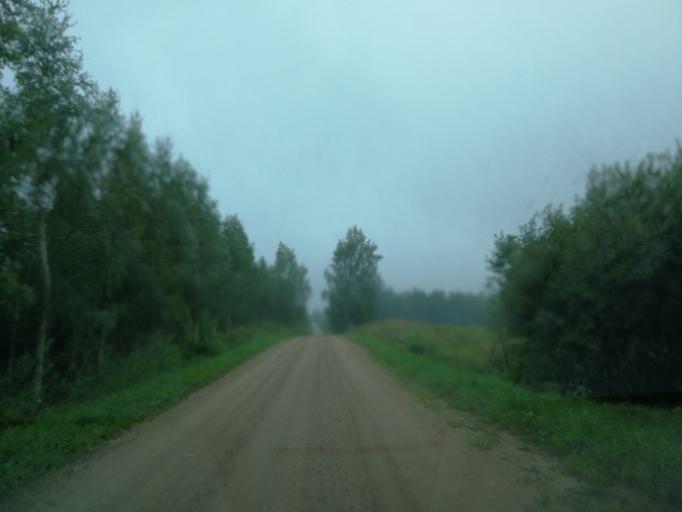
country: LV
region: Preilu Rajons
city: Jaunaglona
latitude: 56.3202
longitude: 27.0169
